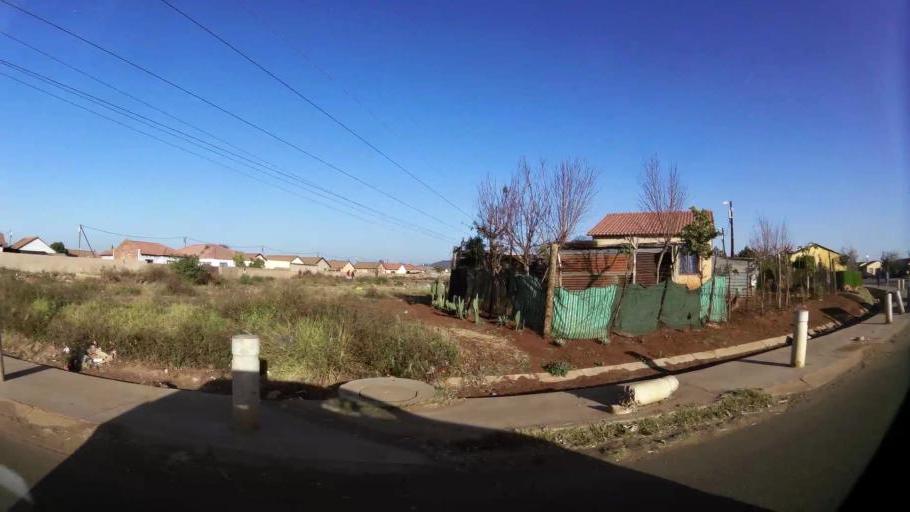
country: ZA
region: Gauteng
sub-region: City of Tshwane Metropolitan Municipality
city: Mabopane
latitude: -25.5965
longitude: 28.1047
